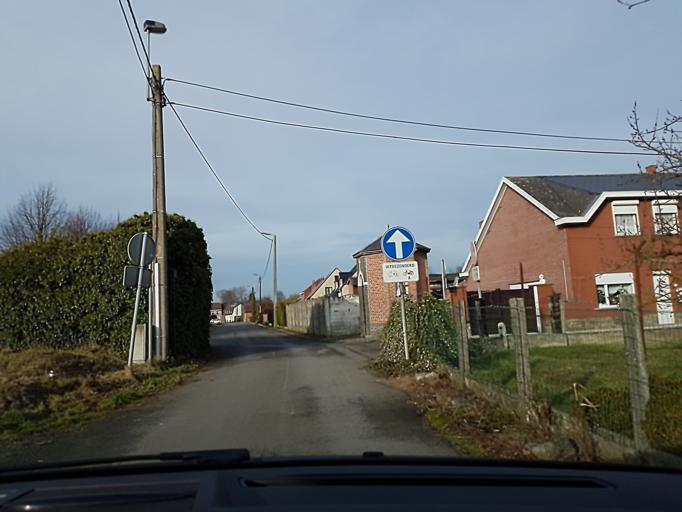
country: BE
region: Flanders
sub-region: Provincie Vlaams-Brabant
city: Haacht
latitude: 50.9407
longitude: 4.6461
